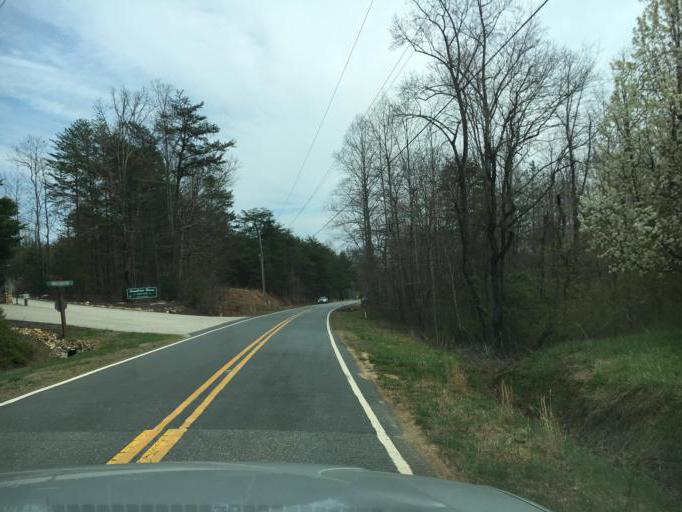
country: US
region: North Carolina
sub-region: Rutherford County
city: Lake Lure
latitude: 35.4830
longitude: -82.1249
